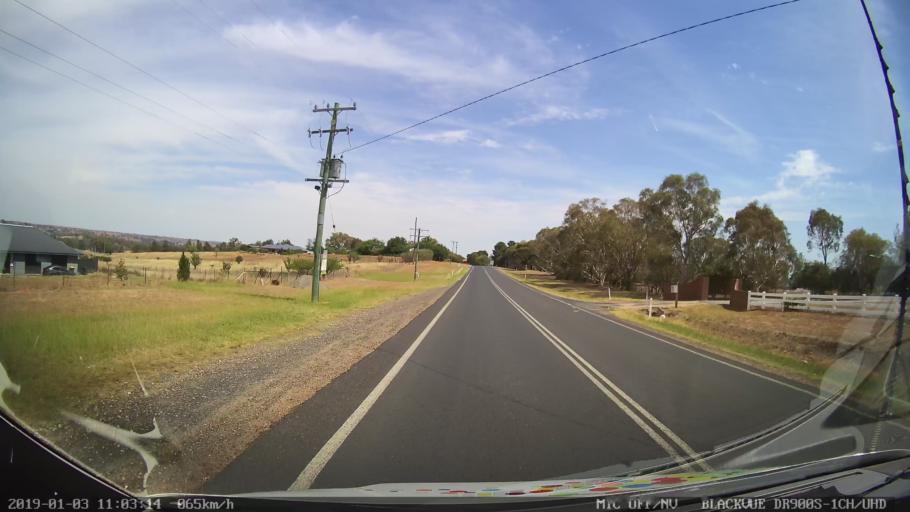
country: AU
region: New South Wales
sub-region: Young
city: Young
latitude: -34.2922
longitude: 148.2959
